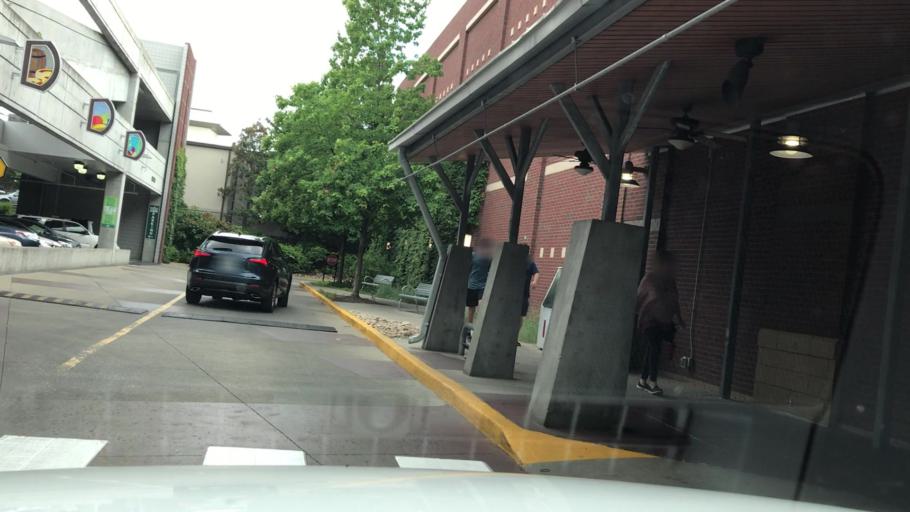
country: US
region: Tennessee
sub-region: Davidson County
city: Oak Hill
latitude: 36.1032
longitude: -86.8184
